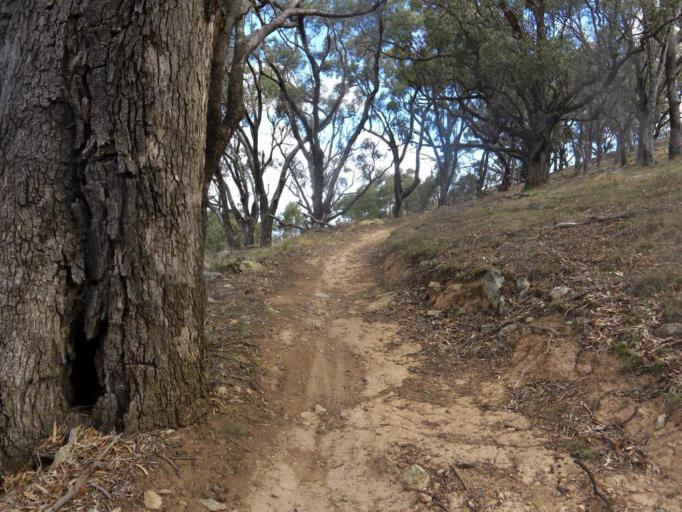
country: AU
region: Australian Capital Territory
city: Belconnen
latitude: -35.1399
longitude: 149.0934
